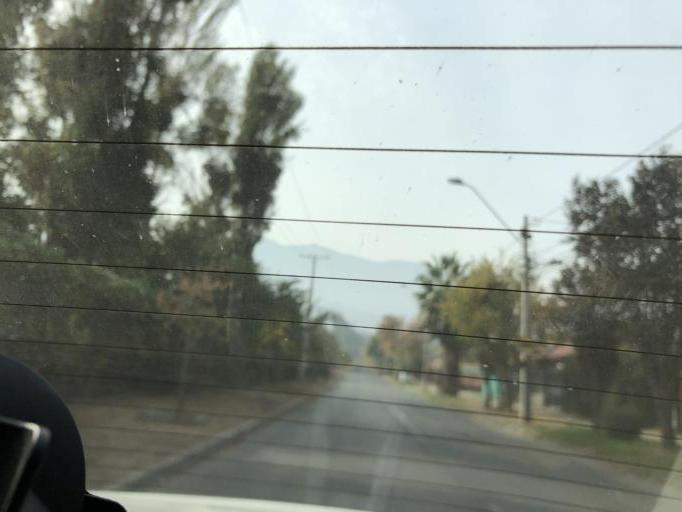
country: CL
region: Santiago Metropolitan
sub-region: Provincia de Cordillera
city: Puente Alto
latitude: -33.5479
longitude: -70.5592
